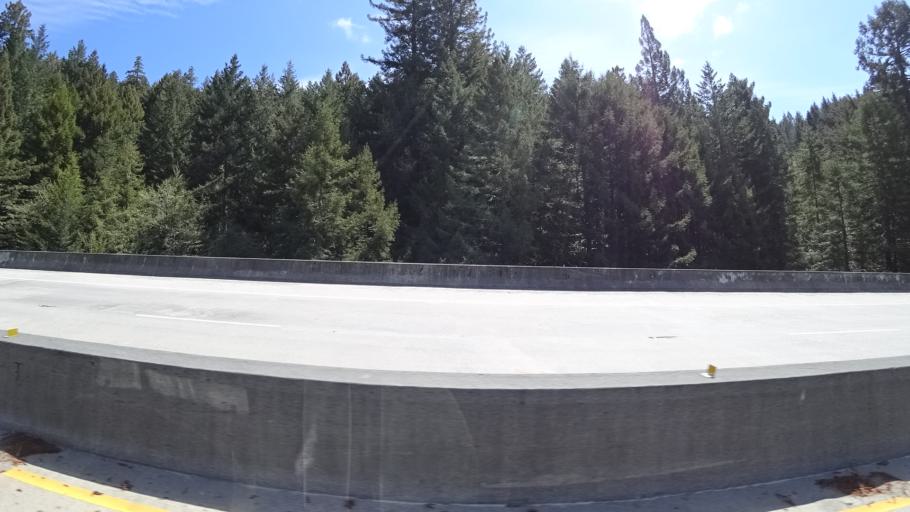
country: US
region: California
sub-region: Humboldt County
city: Westhaven-Moonstone
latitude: 41.3712
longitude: -123.9906
